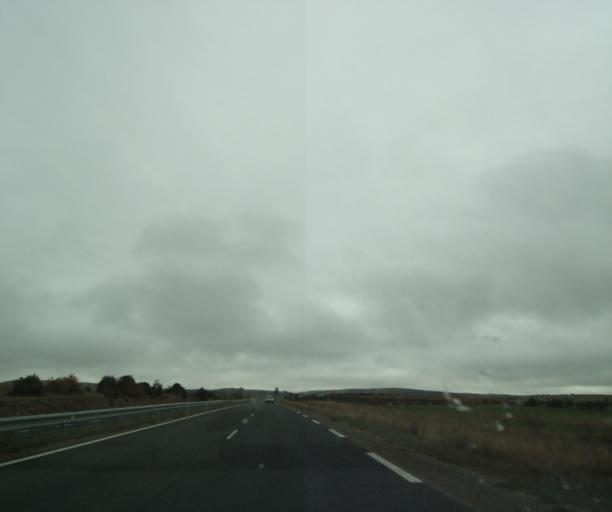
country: FR
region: Midi-Pyrenees
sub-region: Departement de l'Aveyron
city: Millau
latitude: 44.0740
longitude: 3.1125
